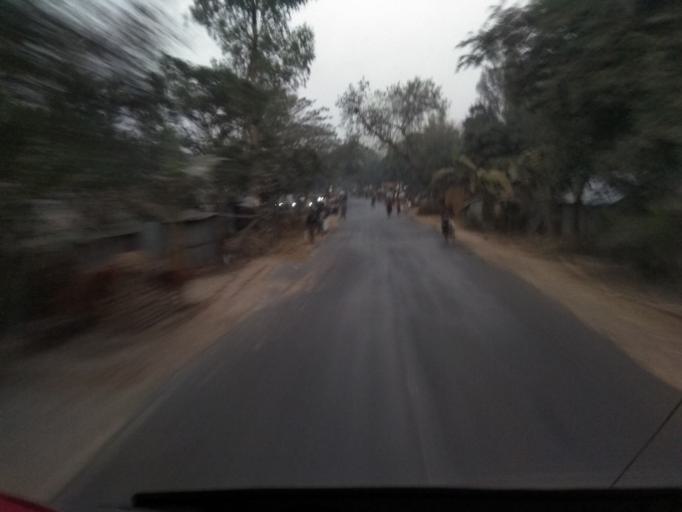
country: BD
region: Rajshahi
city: Bogra
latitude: 24.7501
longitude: 89.3423
